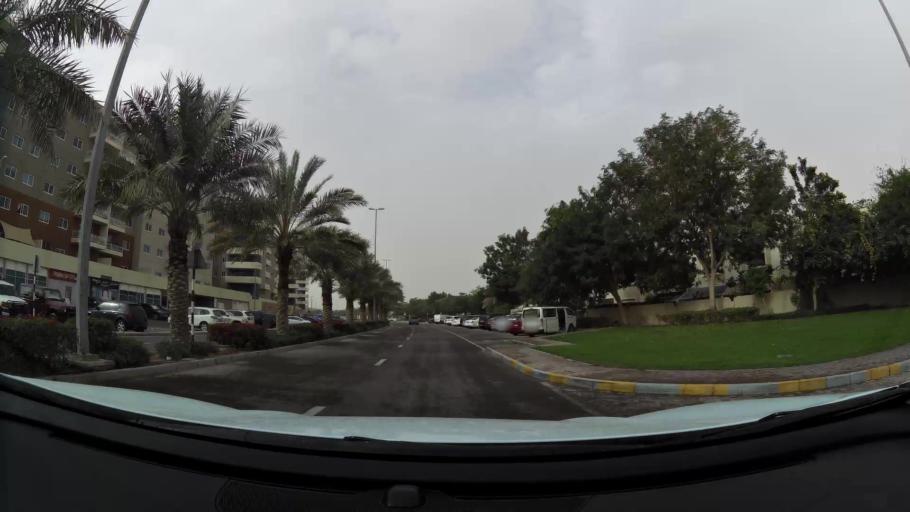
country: AE
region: Abu Dhabi
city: Abu Dhabi
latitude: 24.4582
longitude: 54.6733
